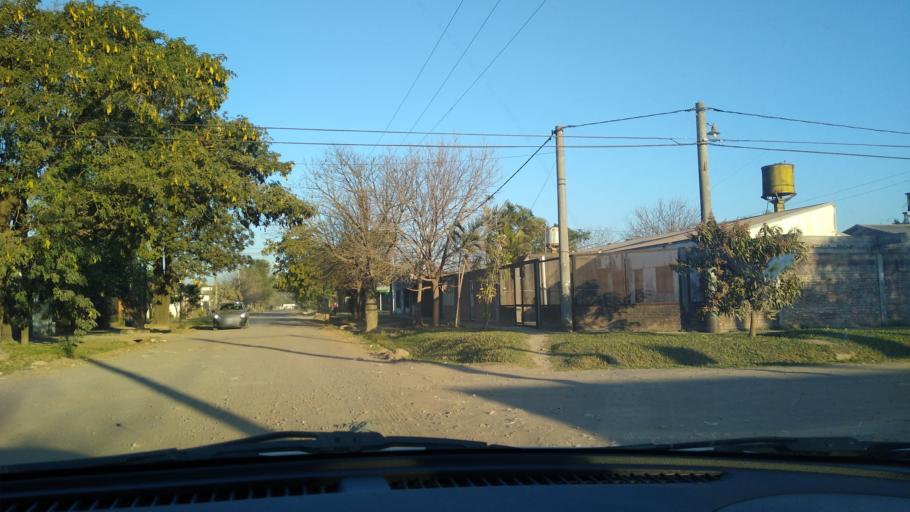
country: AR
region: Chaco
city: Resistencia
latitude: -27.4873
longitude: -58.9770
